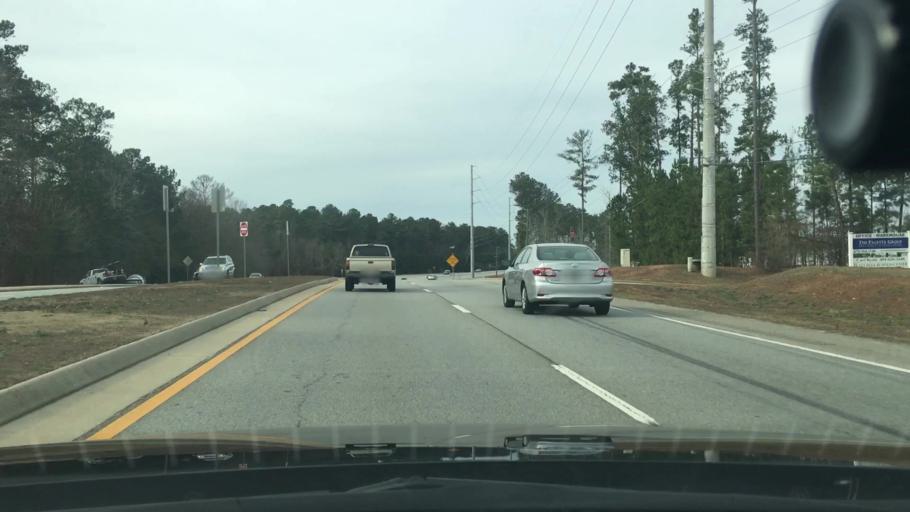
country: US
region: Georgia
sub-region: Coweta County
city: Senoia
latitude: 33.3435
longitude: -84.5442
